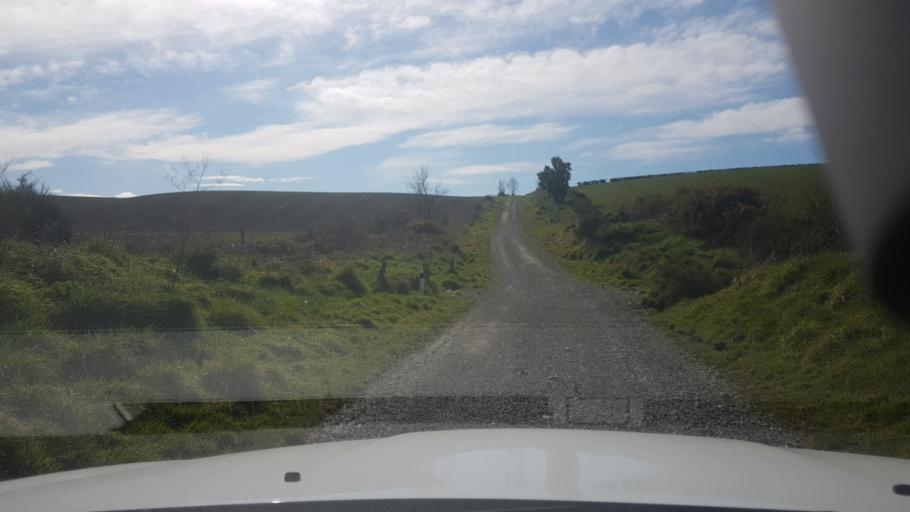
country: NZ
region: Canterbury
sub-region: Timaru District
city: Pleasant Point
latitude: -44.2017
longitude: 171.1869
